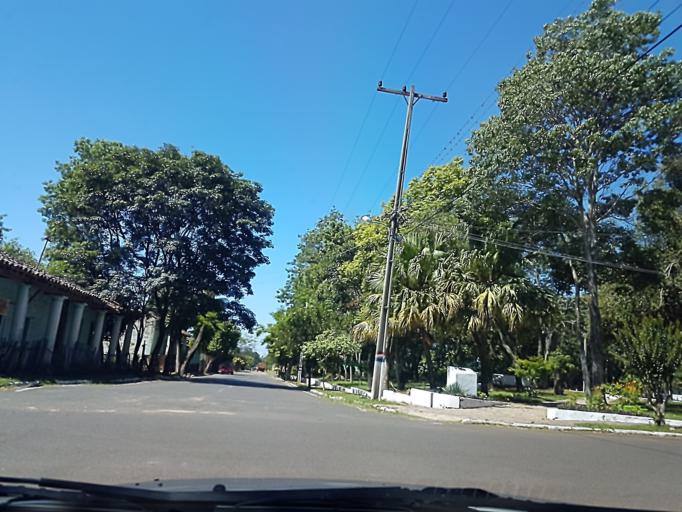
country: PY
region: Cordillera
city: Atyra
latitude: -25.2771
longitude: -57.1725
